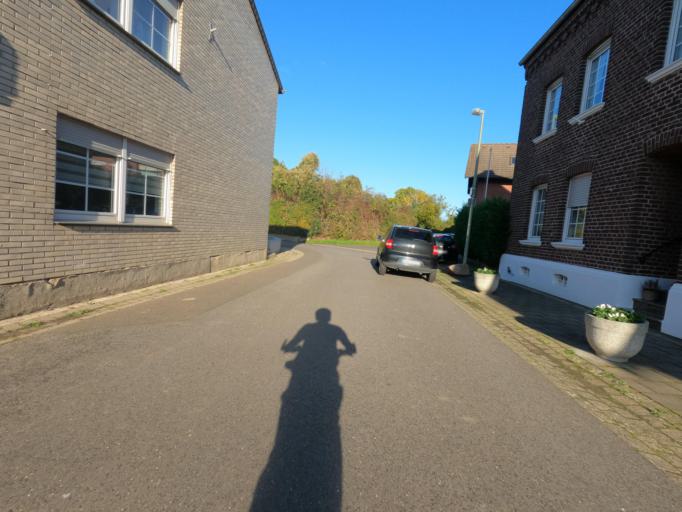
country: DE
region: North Rhine-Westphalia
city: Erkelenz
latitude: 51.0910
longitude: 6.3422
